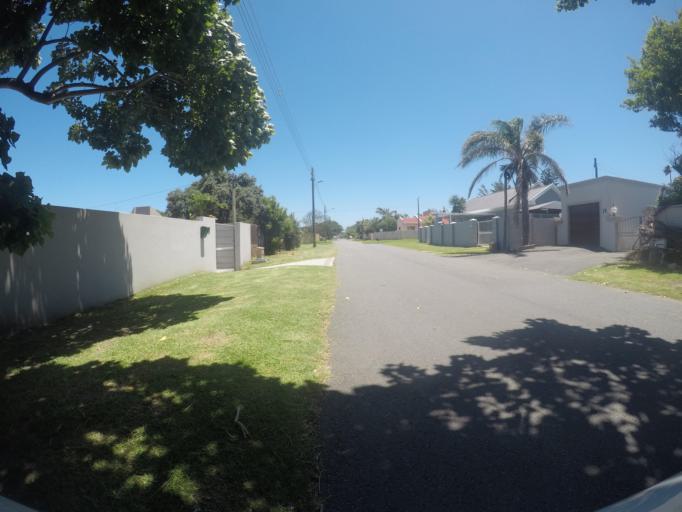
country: ZA
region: Eastern Cape
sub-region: Buffalo City Metropolitan Municipality
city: East London
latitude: -32.9500
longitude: 28.0126
